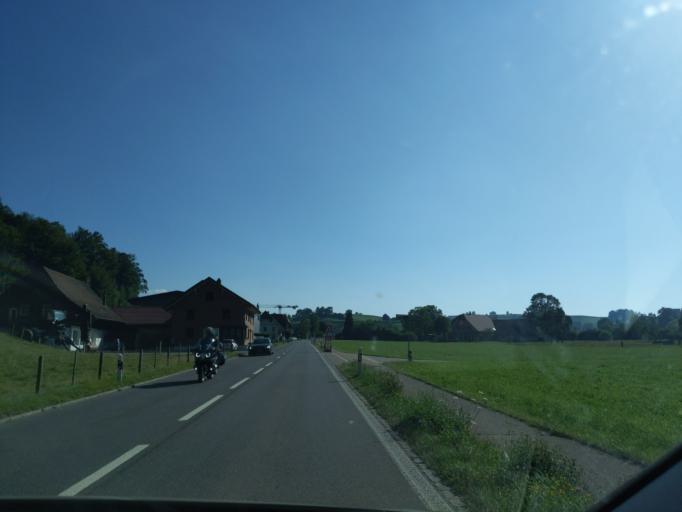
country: CH
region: Lucerne
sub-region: Willisau District
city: Zell
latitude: 47.1319
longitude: 7.9121
